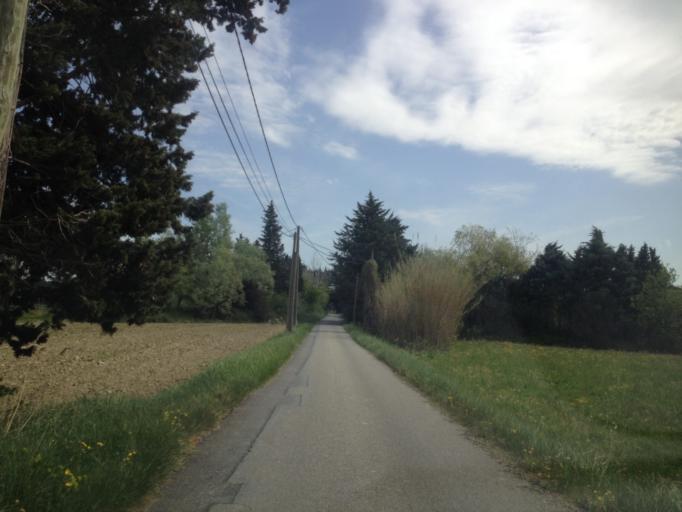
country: FR
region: Provence-Alpes-Cote d'Azur
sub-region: Departement du Vaucluse
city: Caderousse
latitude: 44.1155
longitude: 4.7818
